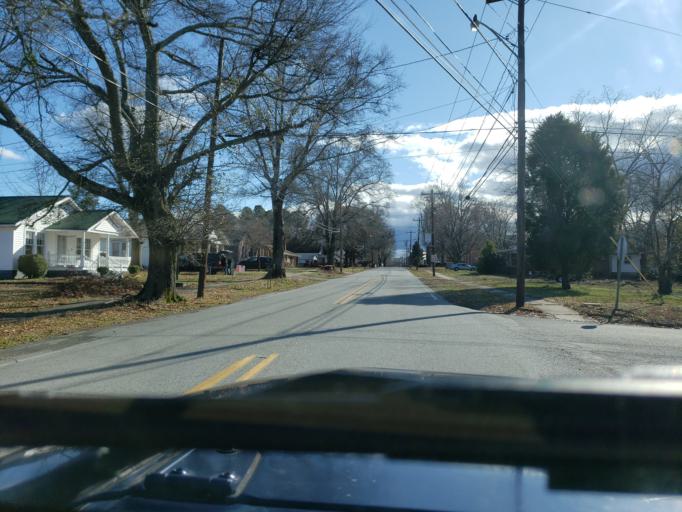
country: US
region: North Carolina
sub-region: Cleveland County
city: White Plains
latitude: 35.1742
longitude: -81.4497
